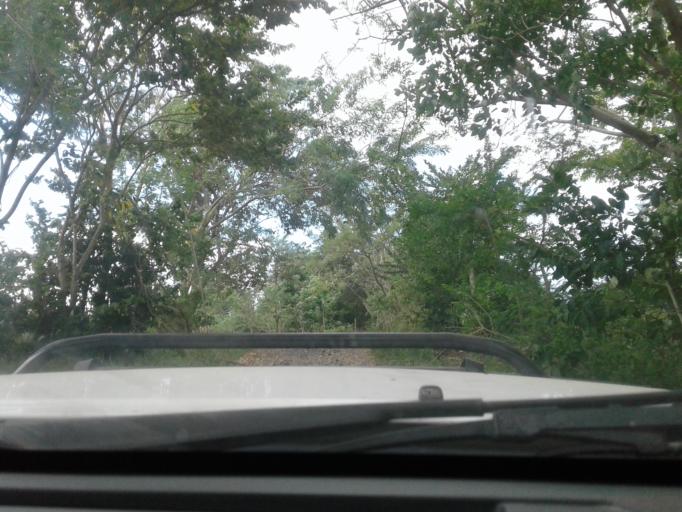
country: NI
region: Rivas
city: Altagracia
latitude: 11.4997
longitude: -85.5591
